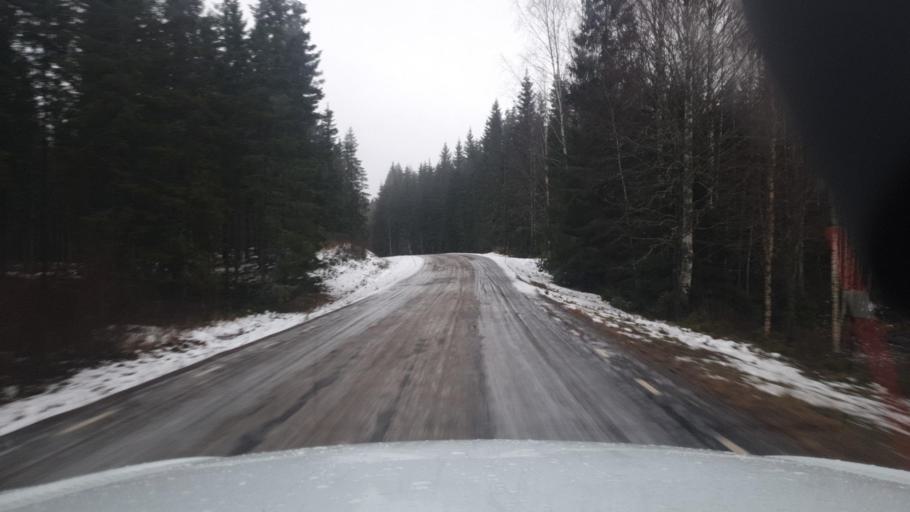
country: SE
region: Vaermland
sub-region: Torsby Kommun
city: Torsby
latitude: 60.0004
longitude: 12.7331
